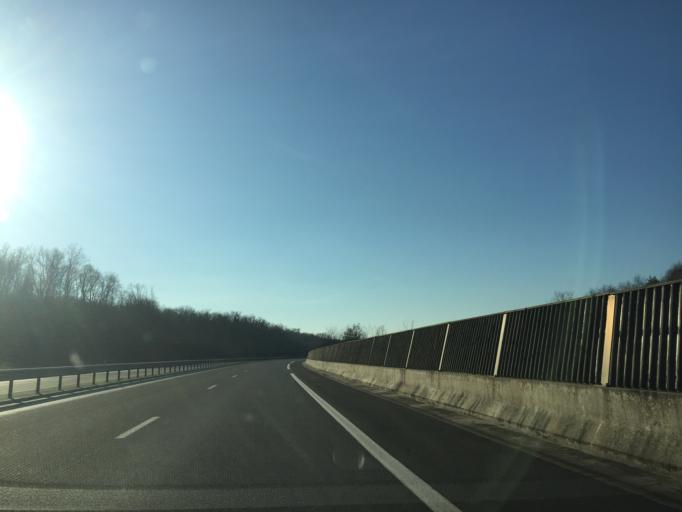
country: FR
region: Limousin
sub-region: Departement de la Correze
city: Mansac
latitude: 45.1575
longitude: 1.3927
